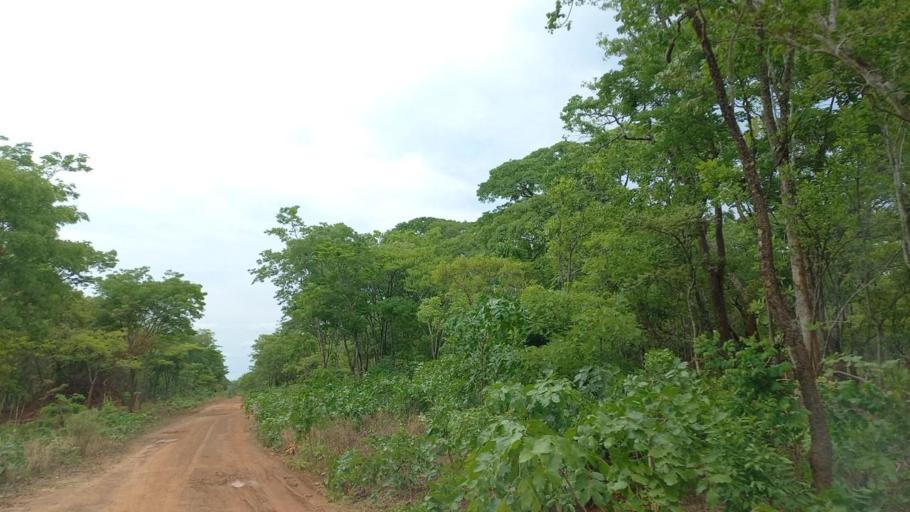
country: ZM
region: North-Western
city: Kalengwa
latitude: -13.5756
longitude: 24.9708
